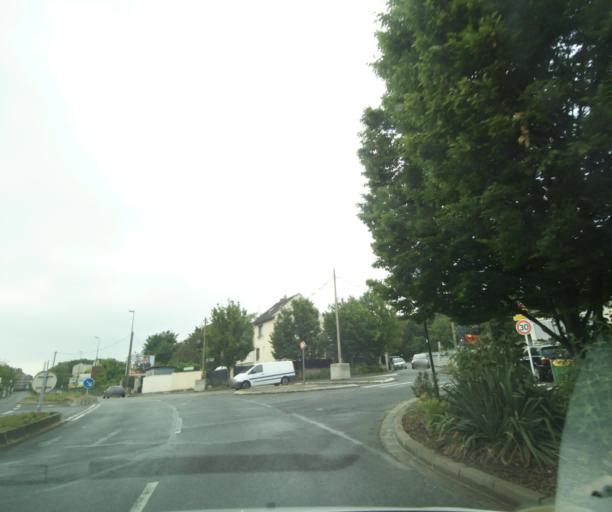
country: FR
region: Ile-de-France
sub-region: Departement du Val-d'Oise
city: Saint-Gratien
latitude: 48.9591
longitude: 2.2792
